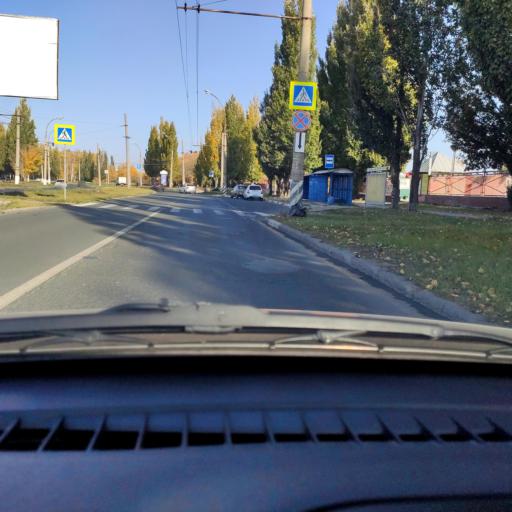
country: RU
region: Samara
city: Tol'yatti
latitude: 53.5410
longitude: 49.2792
